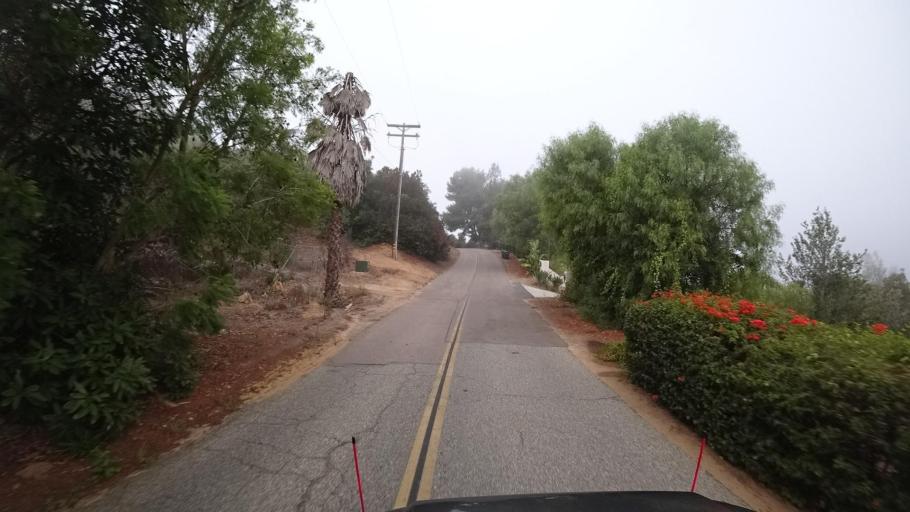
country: US
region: California
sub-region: San Diego County
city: Rainbow
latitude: 33.3504
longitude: -117.1785
